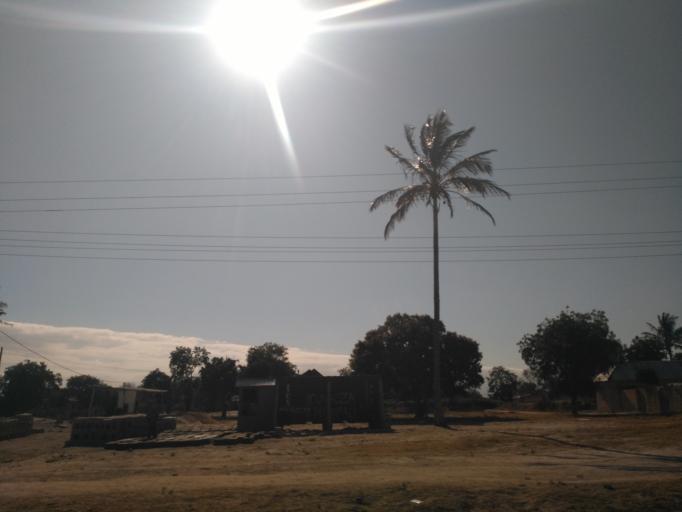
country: TZ
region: Dodoma
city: Dodoma
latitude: -6.1093
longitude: 35.7481
